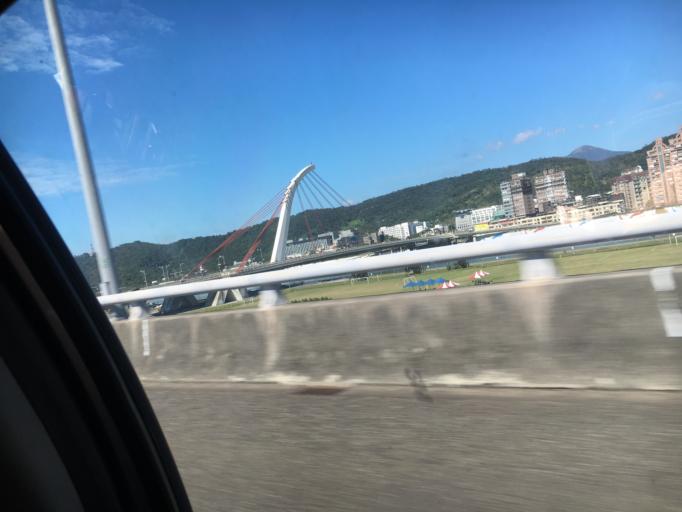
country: TW
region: Taipei
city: Taipei
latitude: 25.0734
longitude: 121.5467
